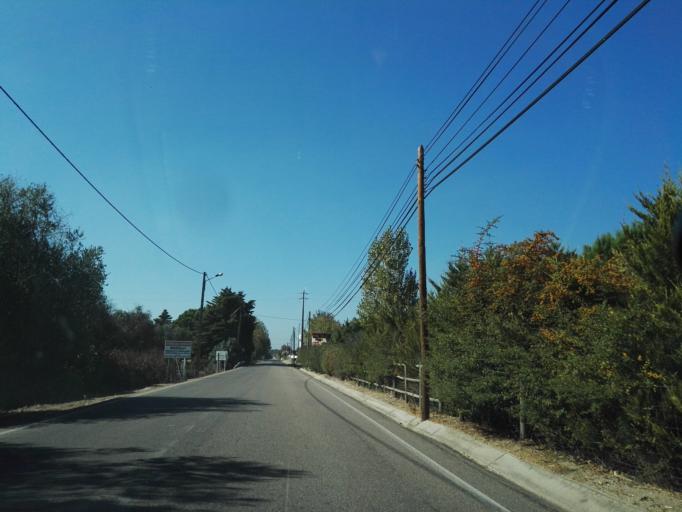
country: PT
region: Santarem
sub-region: Benavente
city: Poceirao
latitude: 38.8578
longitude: -8.7361
